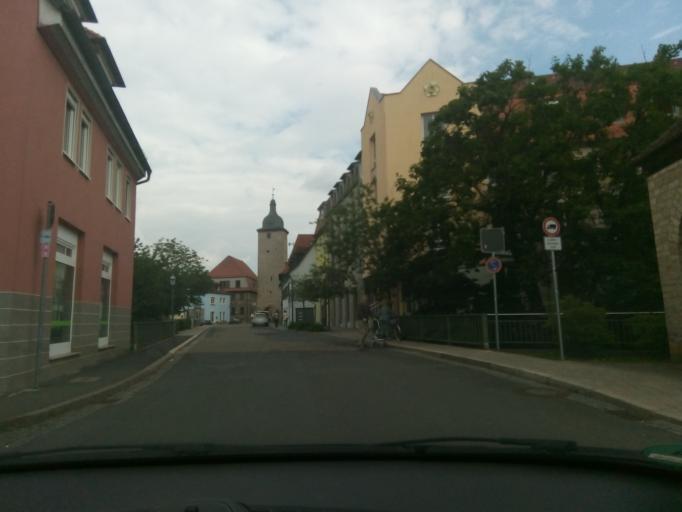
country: DE
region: Bavaria
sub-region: Regierungsbezirk Unterfranken
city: Volkach
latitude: 49.8678
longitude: 10.2239
